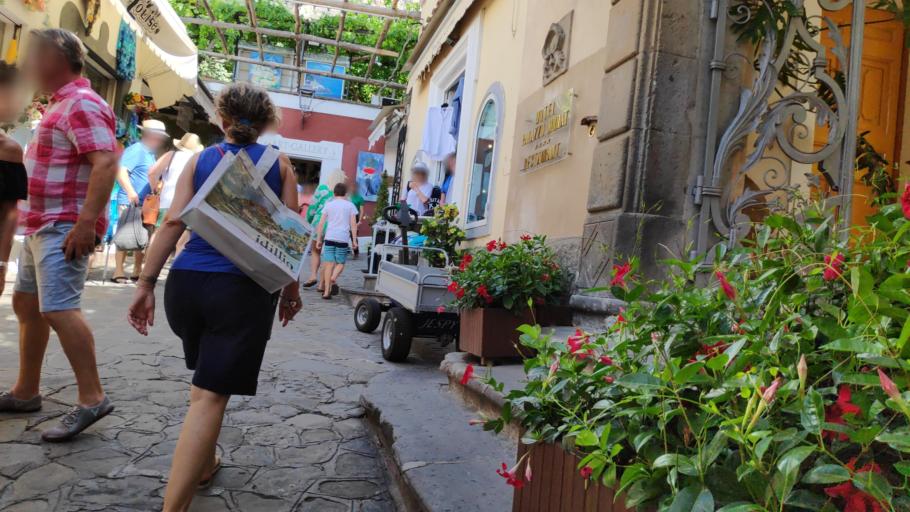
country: IT
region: Campania
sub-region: Provincia di Salerno
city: Positano
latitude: 40.6292
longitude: 14.4866
